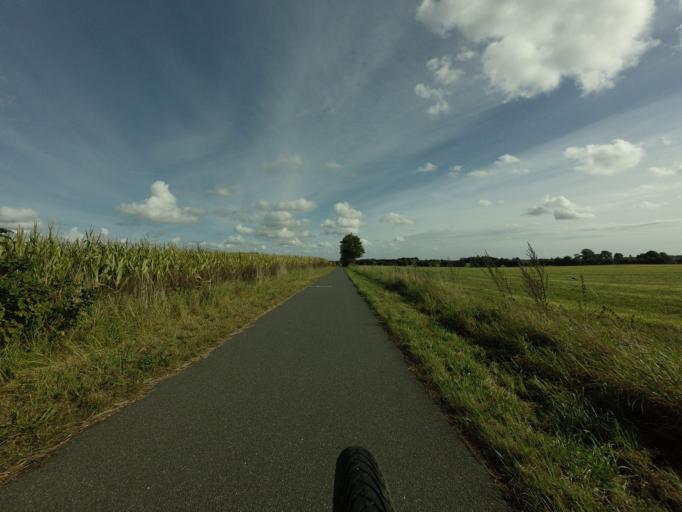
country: DK
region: Central Jutland
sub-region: Viborg Kommune
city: Bjerringbro
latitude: 56.4929
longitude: 9.6617
